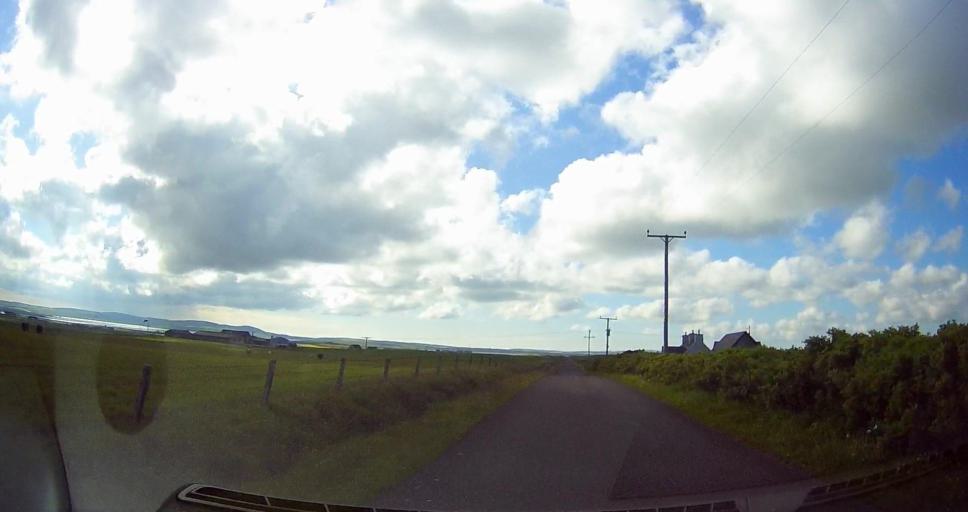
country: GB
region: Scotland
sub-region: Orkney Islands
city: Stromness
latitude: 58.9956
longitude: -3.1615
